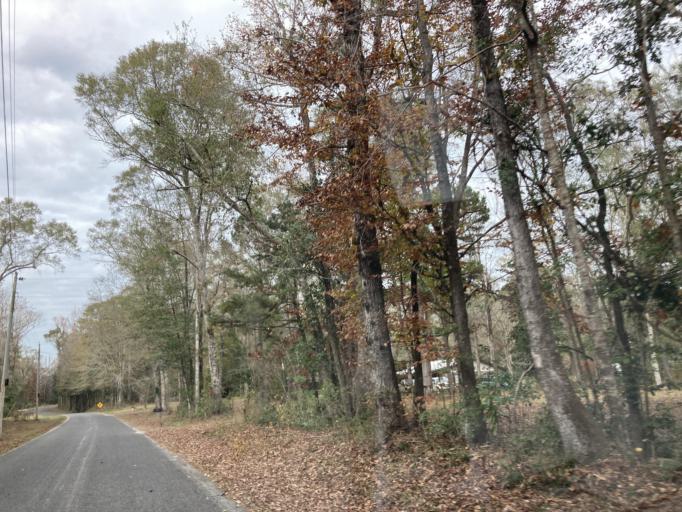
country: US
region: Mississippi
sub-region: Perry County
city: New Augusta
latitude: 31.0716
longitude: -89.1657
